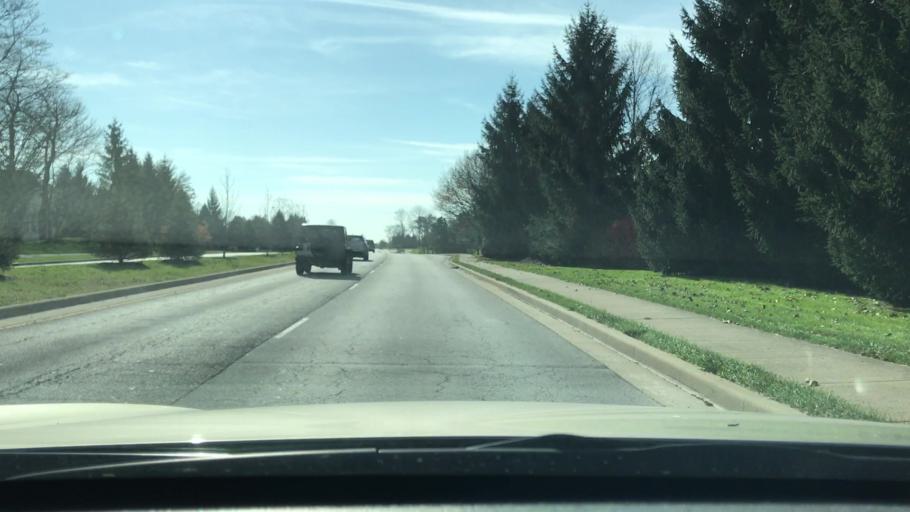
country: US
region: Indiana
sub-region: Hamilton County
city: Carmel
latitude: 39.9880
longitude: -86.0706
